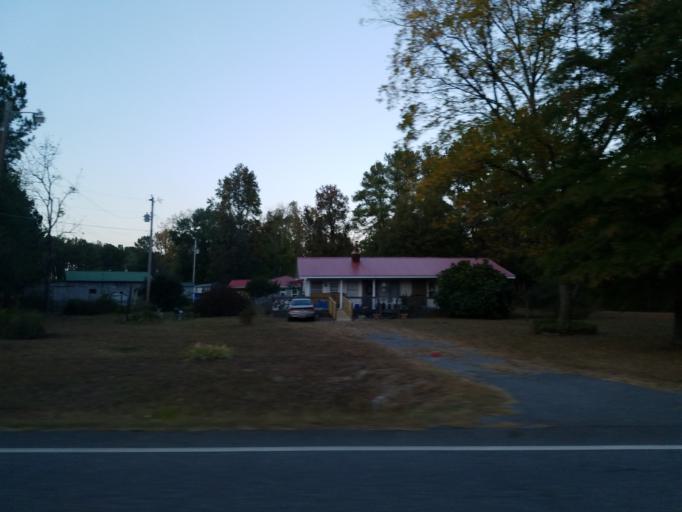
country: US
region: Georgia
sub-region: Gordon County
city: Calhoun
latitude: 34.5749
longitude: -84.9864
